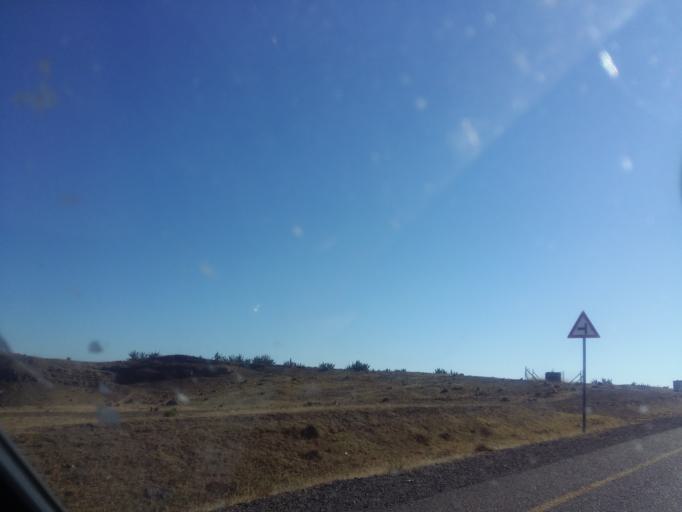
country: LS
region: Mafeteng
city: Mafeteng
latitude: -29.6906
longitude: 27.2793
